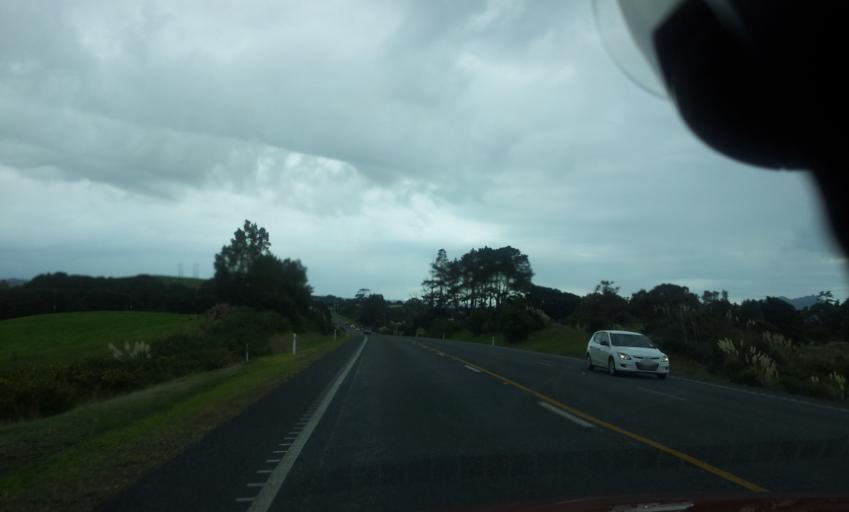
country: NZ
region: Northland
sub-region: Whangarei
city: Ruakaka
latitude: -35.9229
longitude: 174.4534
